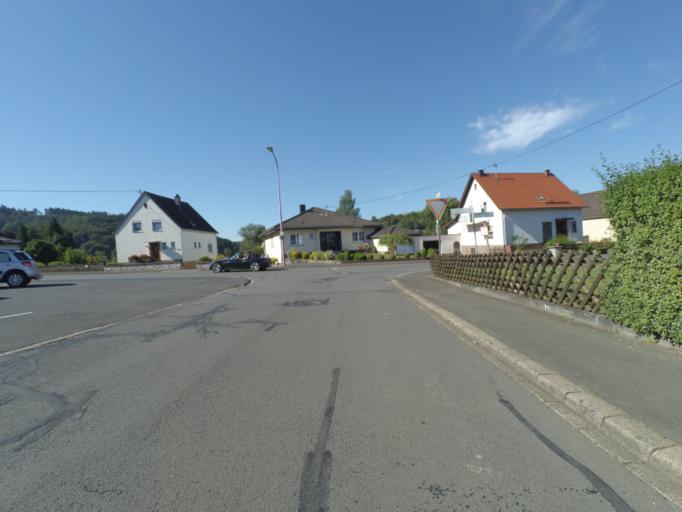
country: DE
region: Rheinland-Pfalz
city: Oberstadtfeld
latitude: 50.1750
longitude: 6.7715
